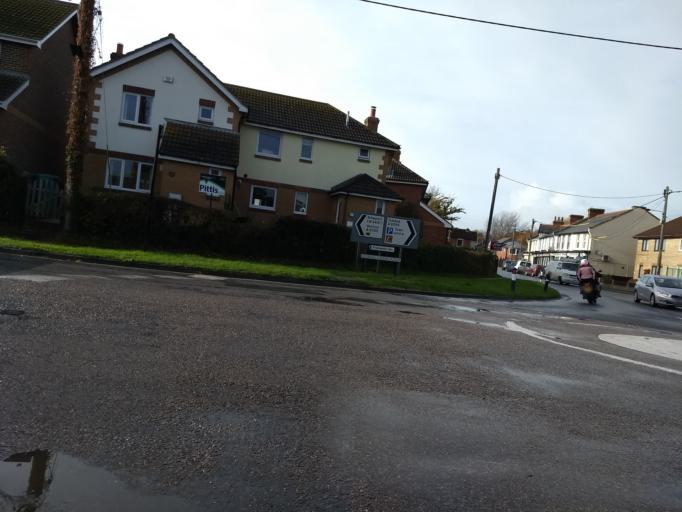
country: GB
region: England
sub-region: Isle of Wight
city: Freshwater
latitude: 50.6821
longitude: -1.5162
